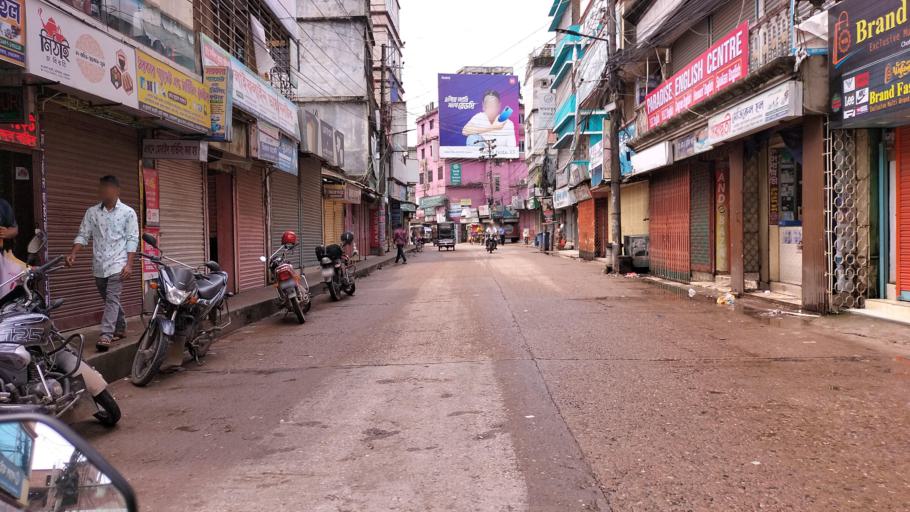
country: BD
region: Dhaka
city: Netrakona
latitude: 24.8834
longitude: 90.7325
